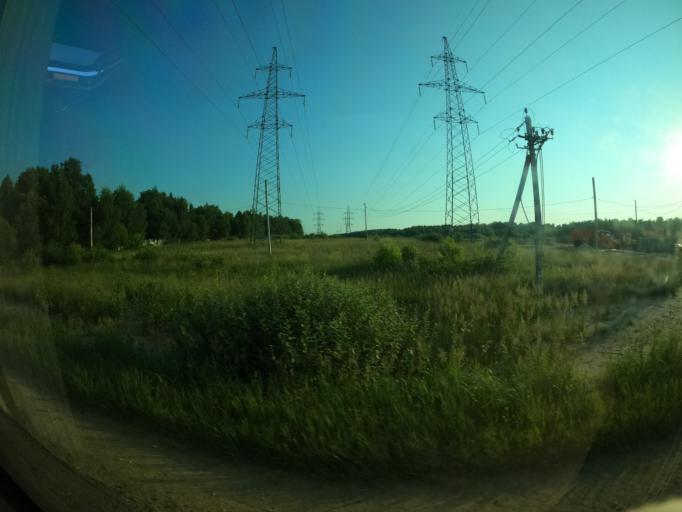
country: RU
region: Moskovskaya
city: Serpukhov
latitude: 54.9485
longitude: 37.3435
